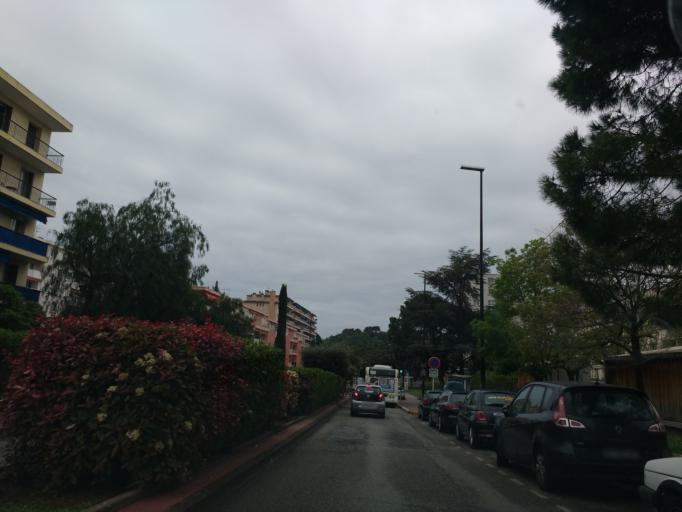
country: FR
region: Provence-Alpes-Cote d'Azur
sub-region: Departement des Alpes-Maritimes
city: Cannes
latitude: 43.5650
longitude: 7.0024
